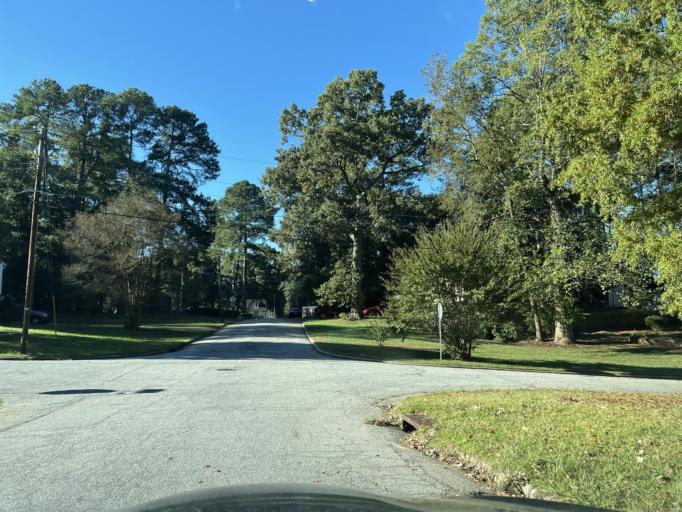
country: US
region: North Carolina
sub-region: Wake County
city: Raleigh
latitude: 35.7498
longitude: -78.6065
